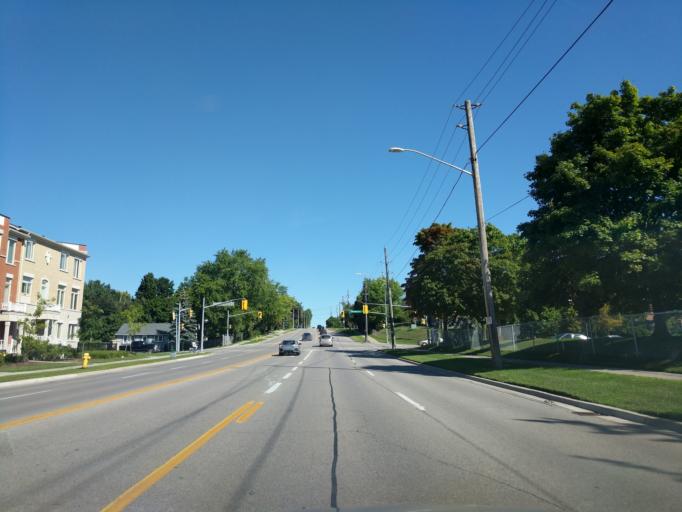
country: CA
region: Ontario
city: Ajax
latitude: 43.8382
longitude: -79.0915
